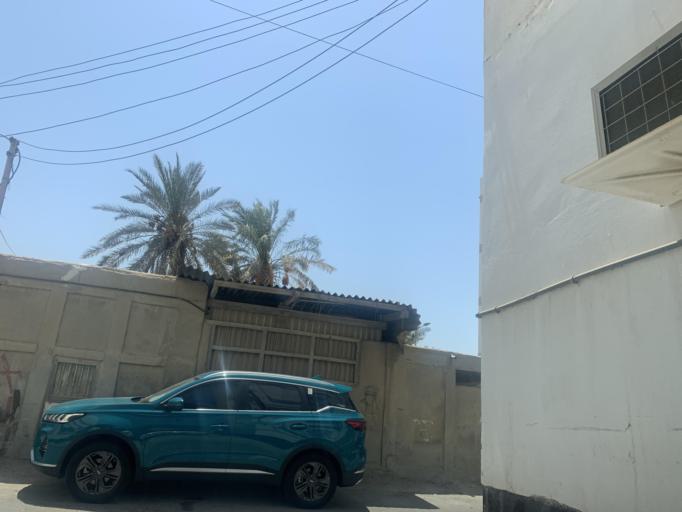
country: BH
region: Muharraq
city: Al Muharraq
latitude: 26.2831
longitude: 50.6208
